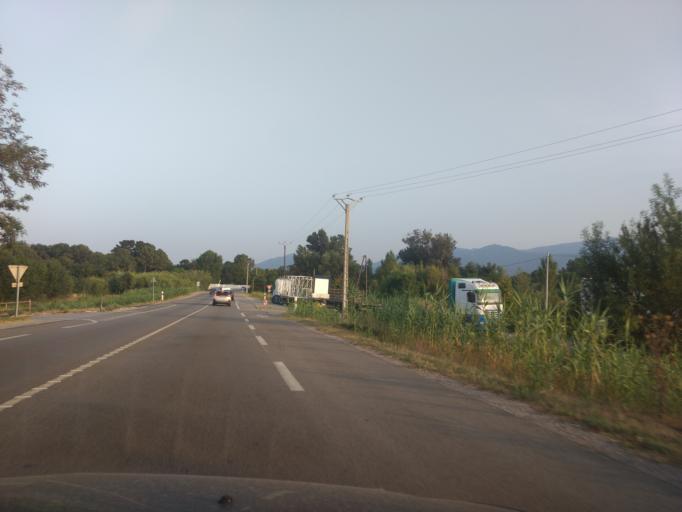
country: FR
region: Languedoc-Roussillon
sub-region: Departement des Pyrenees-Orientales
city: Latour-Bas-Elne
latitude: 42.5838
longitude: 3.0314
